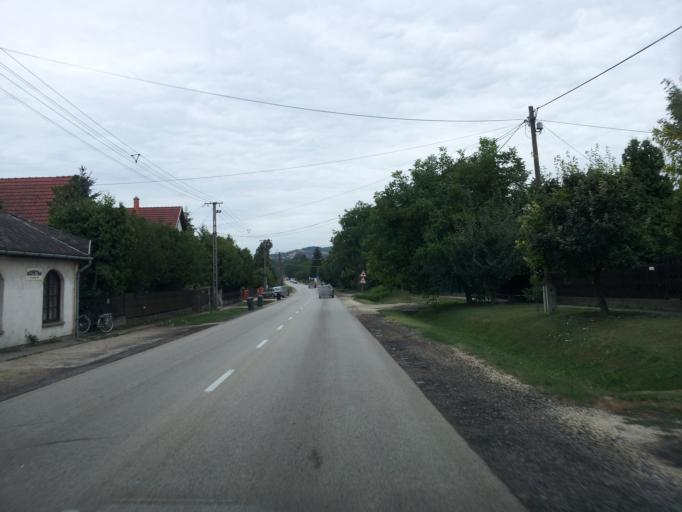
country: HU
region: Fejer
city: Velence
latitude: 47.2402
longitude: 18.6552
